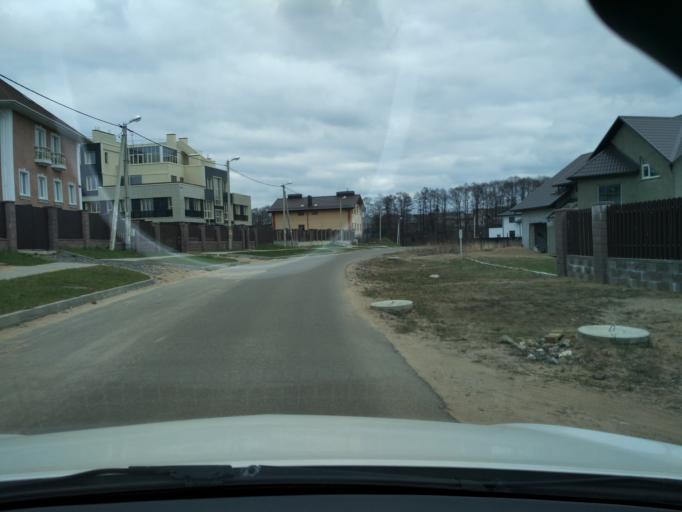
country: BY
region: Minsk
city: Bal'shavik
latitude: 53.9670
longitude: 27.5843
